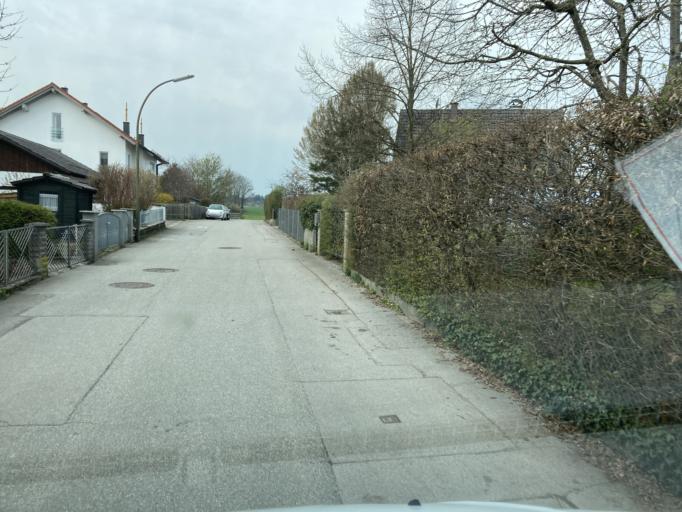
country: DE
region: Bavaria
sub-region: Upper Bavaria
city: Grafing bei Munchen
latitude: 48.0484
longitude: 11.9549
